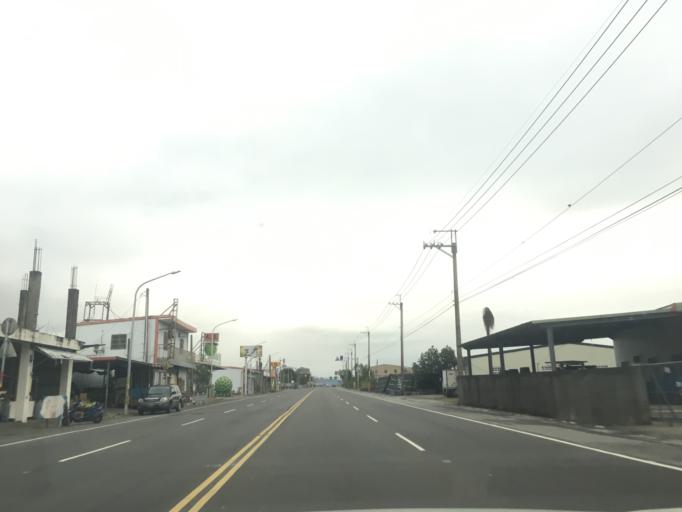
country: TW
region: Taiwan
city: Taitung City
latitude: 22.6859
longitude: 121.0440
